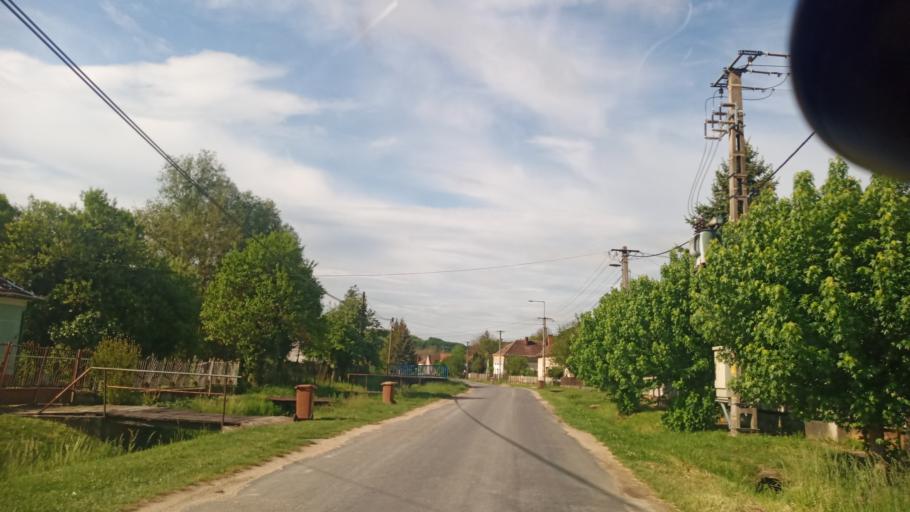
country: HU
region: Zala
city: Pacsa
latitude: 46.6704
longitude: 17.0534
